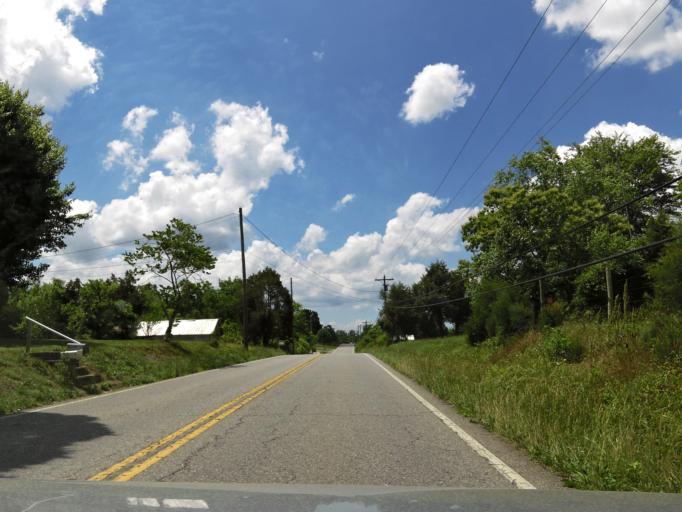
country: US
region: Tennessee
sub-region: Blount County
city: Maryville
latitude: 35.6772
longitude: -84.0426
